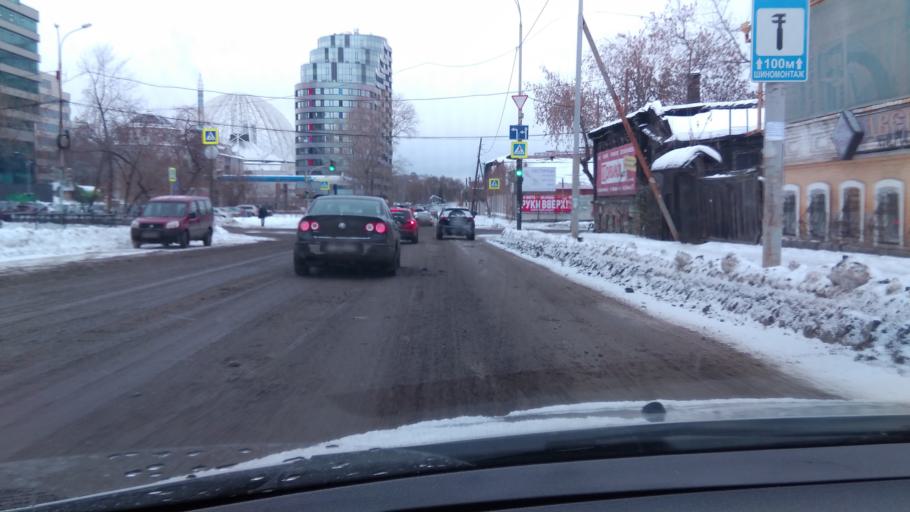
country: RU
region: Sverdlovsk
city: Yekaterinburg
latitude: 56.8225
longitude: 60.6080
